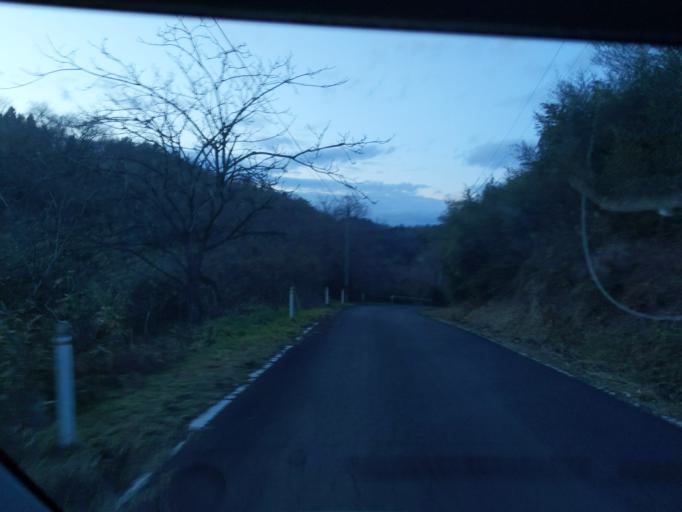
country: JP
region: Iwate
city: Ichinoseki
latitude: 38.8307
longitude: 141.0898
